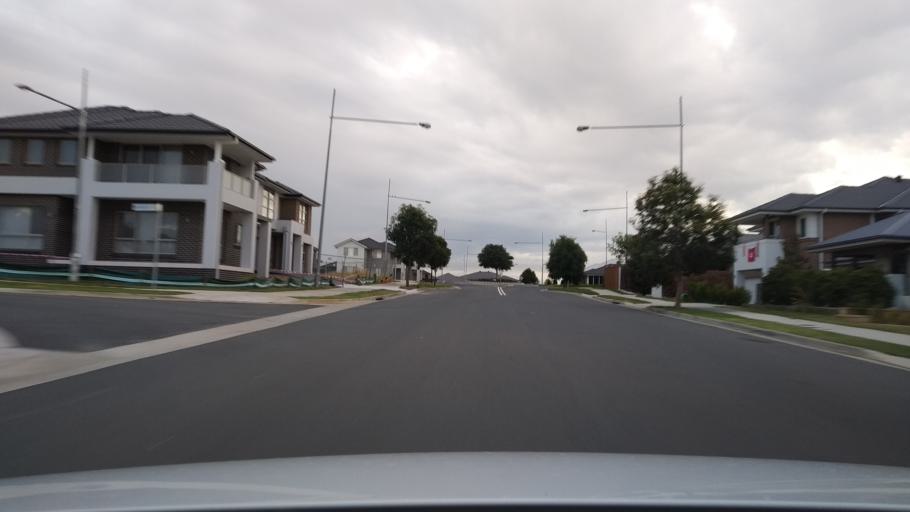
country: AU
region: New South Wales
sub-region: Camden
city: Narellan
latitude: -34.0073
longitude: 150.7362
